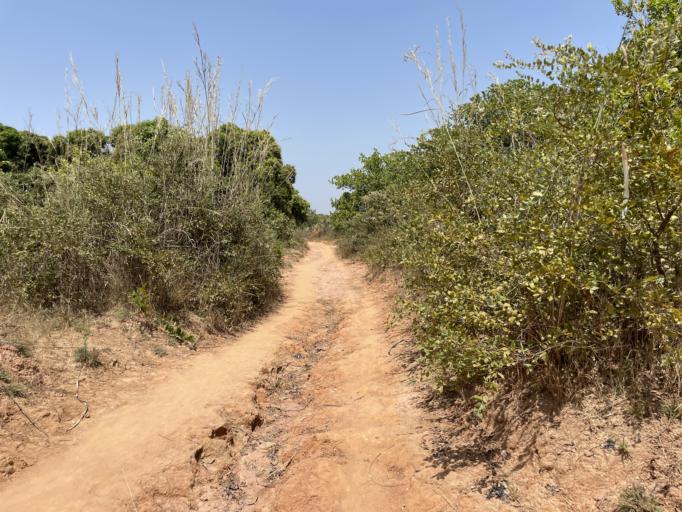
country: GW
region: Oio
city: Bissora
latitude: 12.4378
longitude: -15.6153
